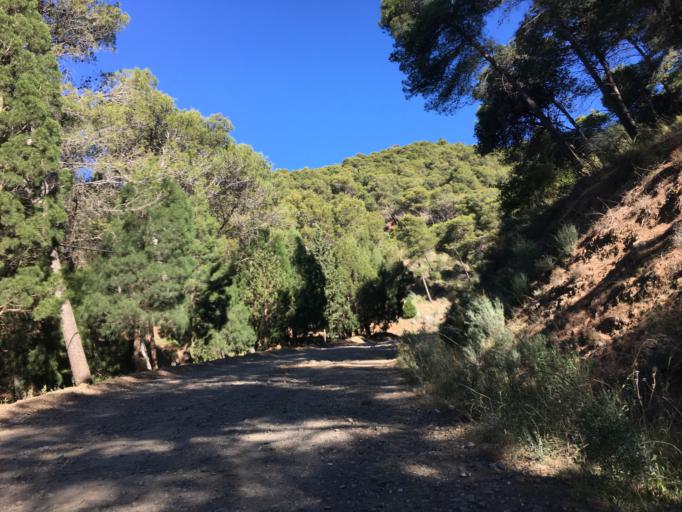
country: ES
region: Andalusia
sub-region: Provincia de Malaga
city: Malaga
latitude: 36.7794
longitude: -4.3852
